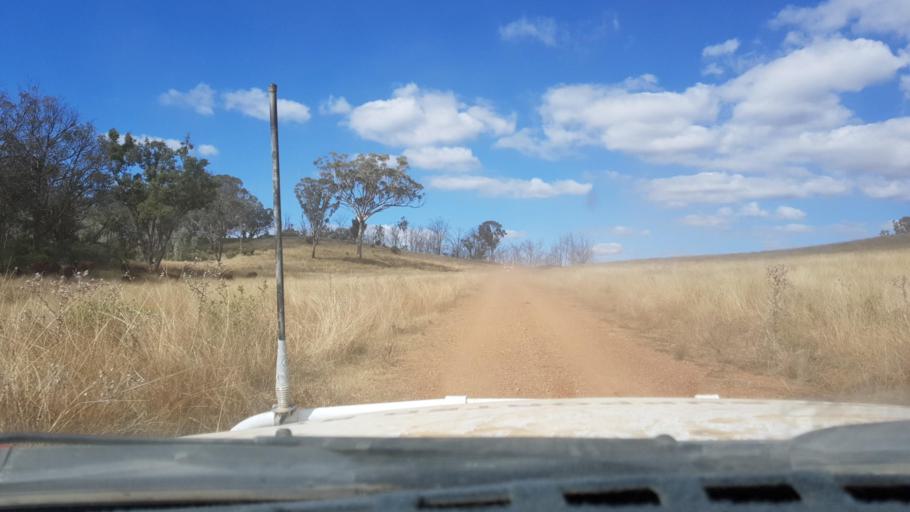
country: AU
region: New South Wales
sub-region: Tamworth Municipality
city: Manilla
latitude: -30.4354
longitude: 150.8267
